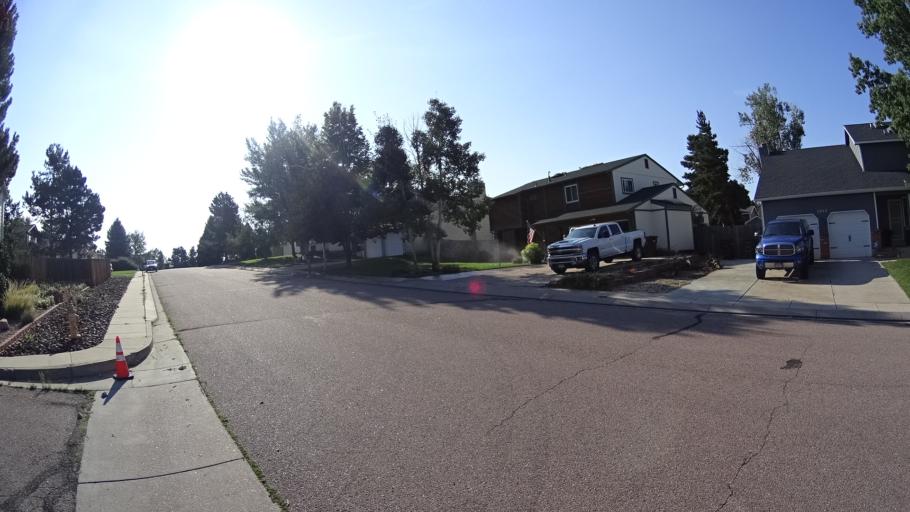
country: US
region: Colorado
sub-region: El Paso County
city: Black Forest
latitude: 38.9451
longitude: -104.7707
